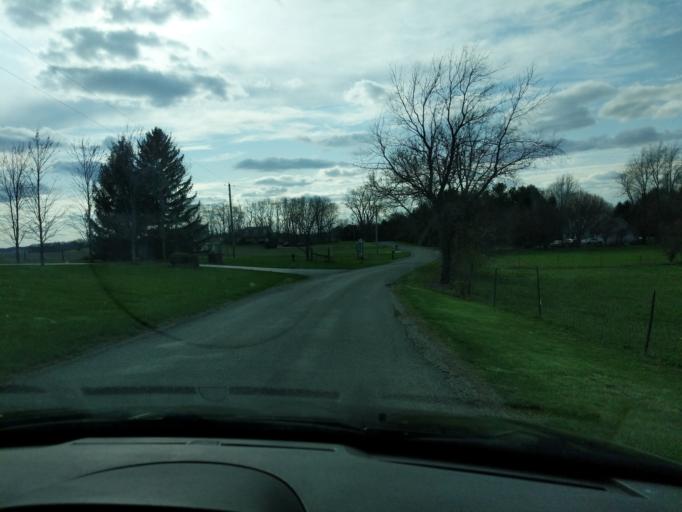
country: US
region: Ohio
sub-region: Champaign County
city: Urbana
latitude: 40.1358
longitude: -83.6785
